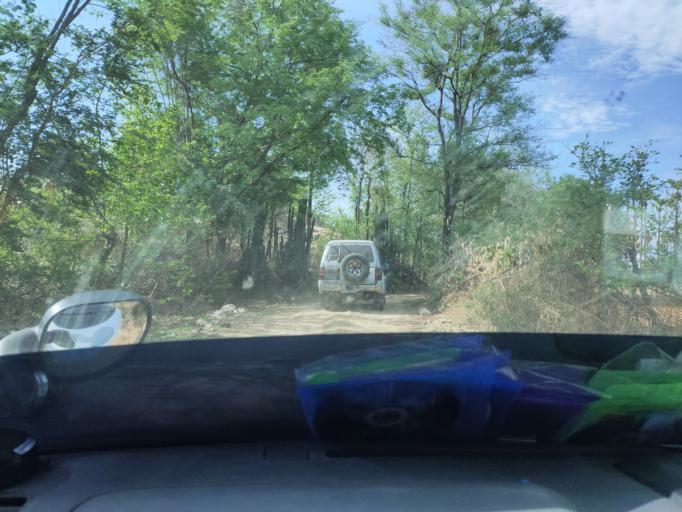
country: MM
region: Magway
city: Chauk
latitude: 20.9580
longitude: 94.9907
